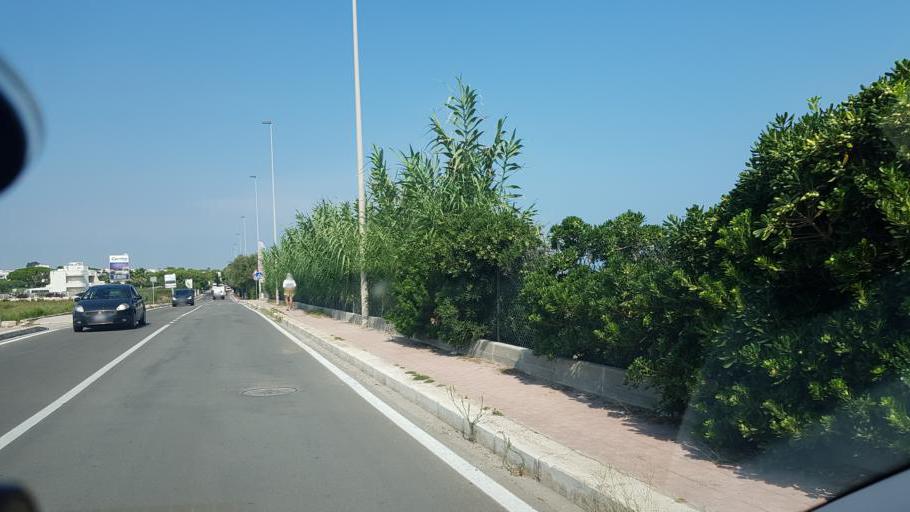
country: IT
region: Apulia
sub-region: Provincia di Brindisi
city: Fasano
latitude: 40.9024
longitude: 17.3559
